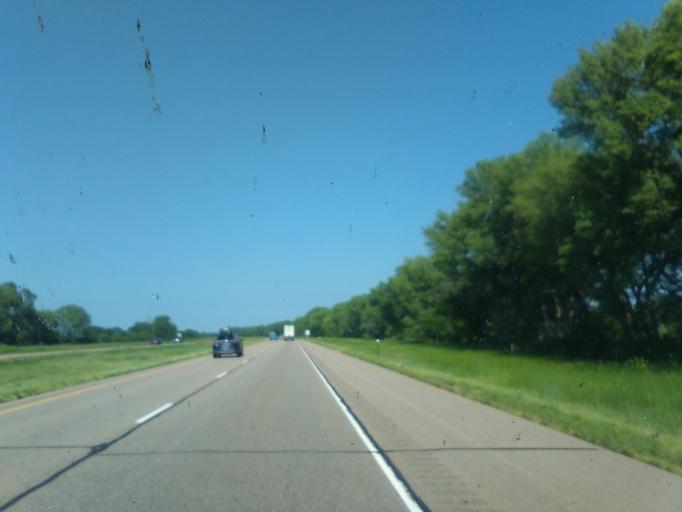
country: US
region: Nebraska
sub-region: Buffalo County
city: Shelton
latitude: 40.7248
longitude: -98.6796
